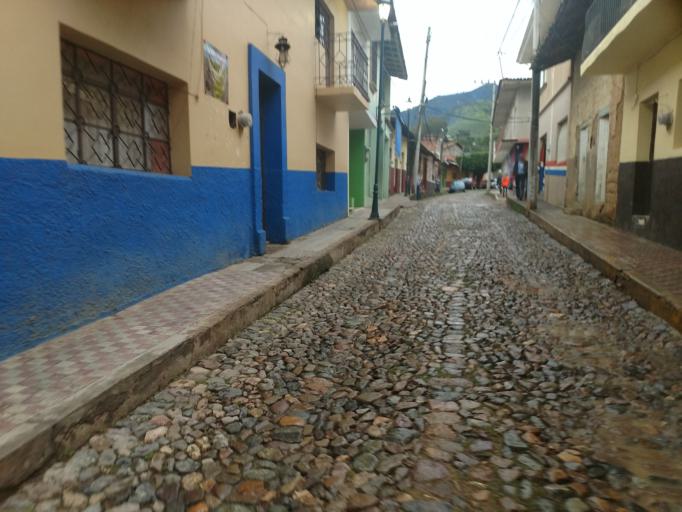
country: MX
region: Jalisco
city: Talpa de Allende
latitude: 20.3801
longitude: -104.8203
